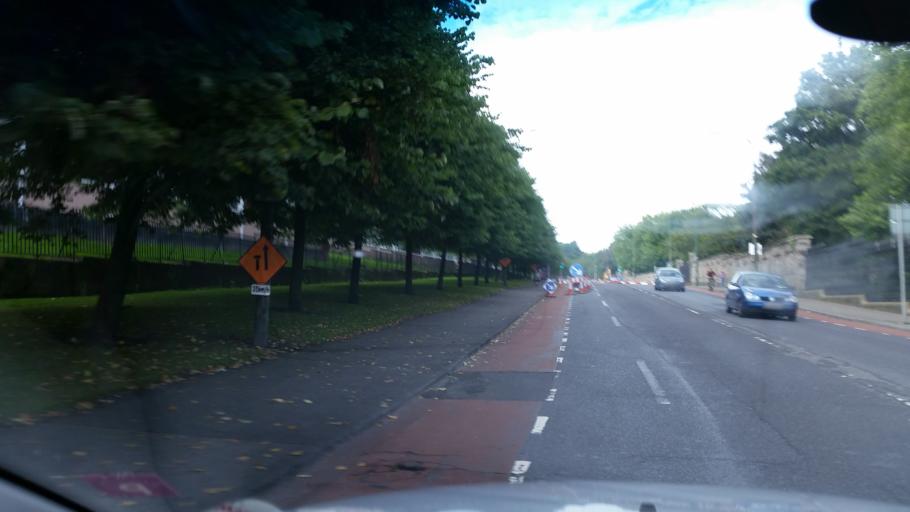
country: IE
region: Leinster
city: Cabra
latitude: 53.3519
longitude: -6.2735
